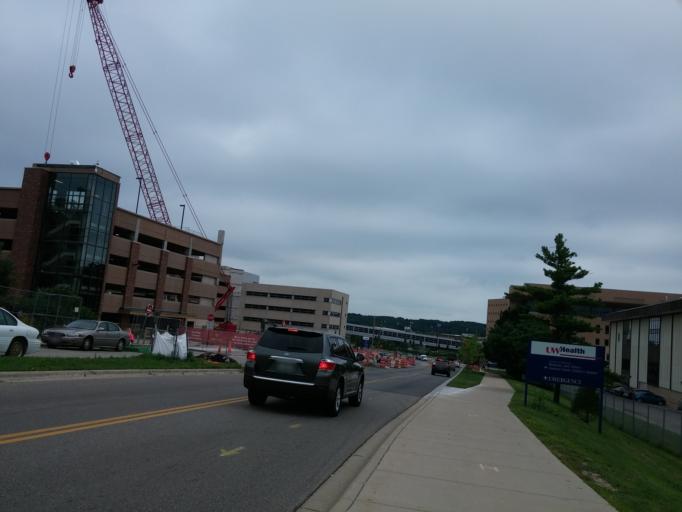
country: US
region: Wisconsin
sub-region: Dane County
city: Shorewood Hills
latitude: 43.0755
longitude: -89.4288
